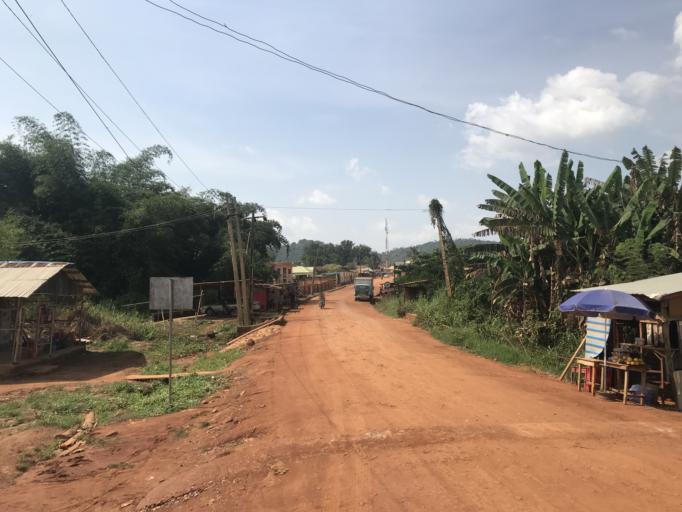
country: NG
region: Osun
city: Ilesa
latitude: 7.6189
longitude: 4.7131
